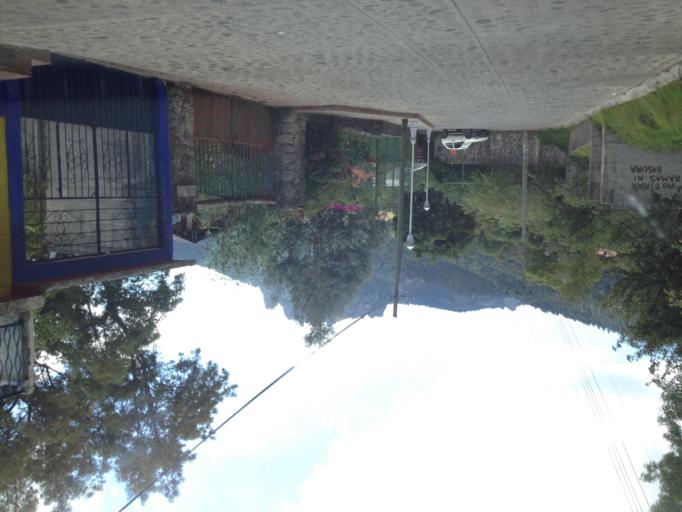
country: MX
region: Hidalgo
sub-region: Pachuca de Soto
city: San Miguel Cerezo (El Cerezo)
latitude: 20.2154
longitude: -98.7278
